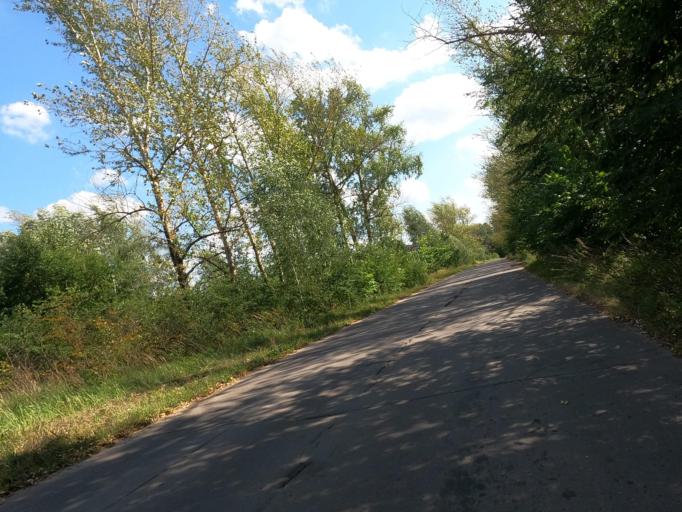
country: RU
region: Moskovskaya
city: Peski
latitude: 55.2249
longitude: 38.7519
